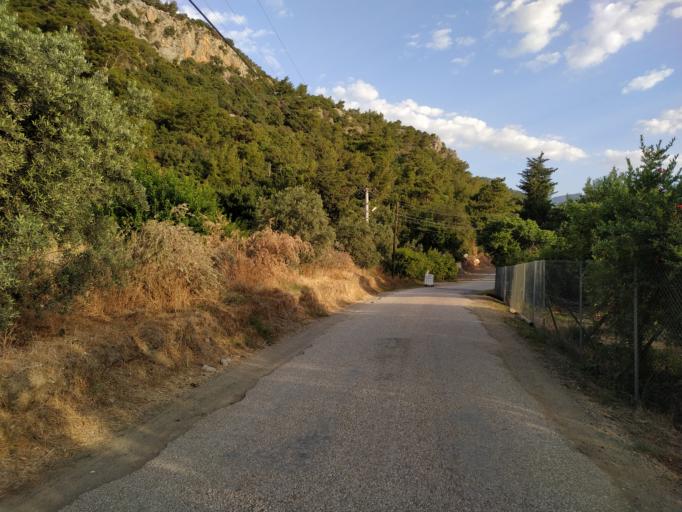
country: TR
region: Antalya
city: Tekirova
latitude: 36.4126
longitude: 30.4732
